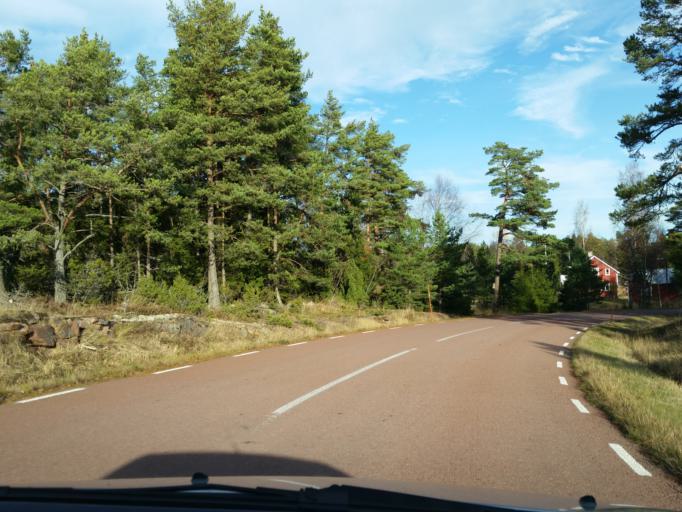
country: AX
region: Alands landsbygd
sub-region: Saltvik
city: Saltvik
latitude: 60.3454
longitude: 20.0888
